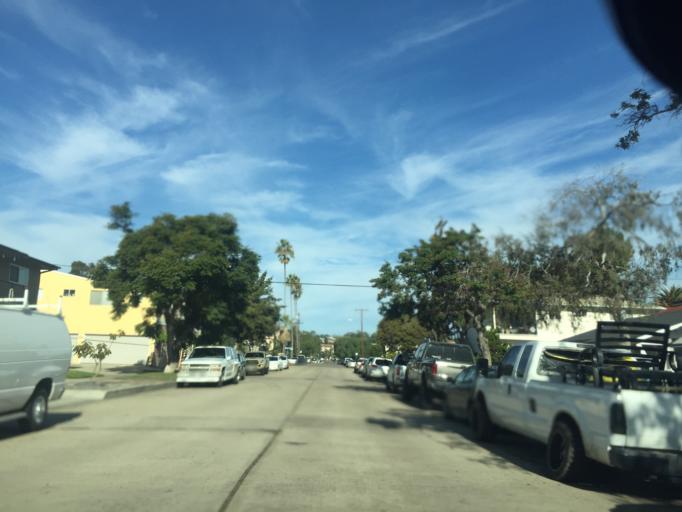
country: US
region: California
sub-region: San Diego County
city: La Jolla
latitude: 32.7960
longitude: -117.2357
